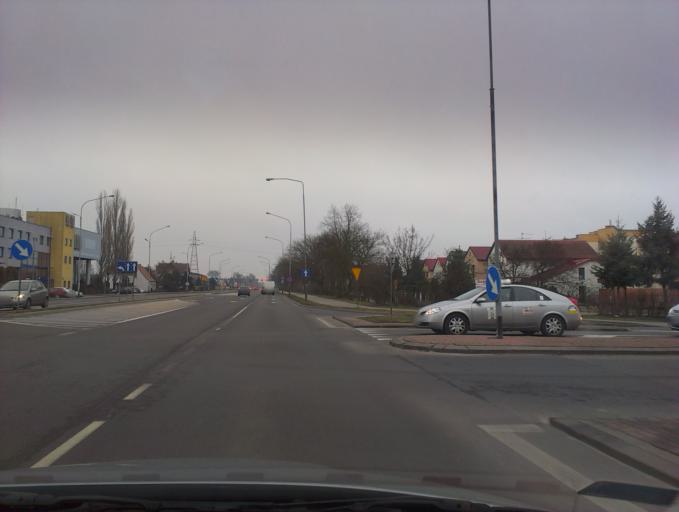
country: PL
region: Greater Poland Voivodeship
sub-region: Powiat pilski
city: Pila
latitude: 53.1350
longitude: 16.7524
